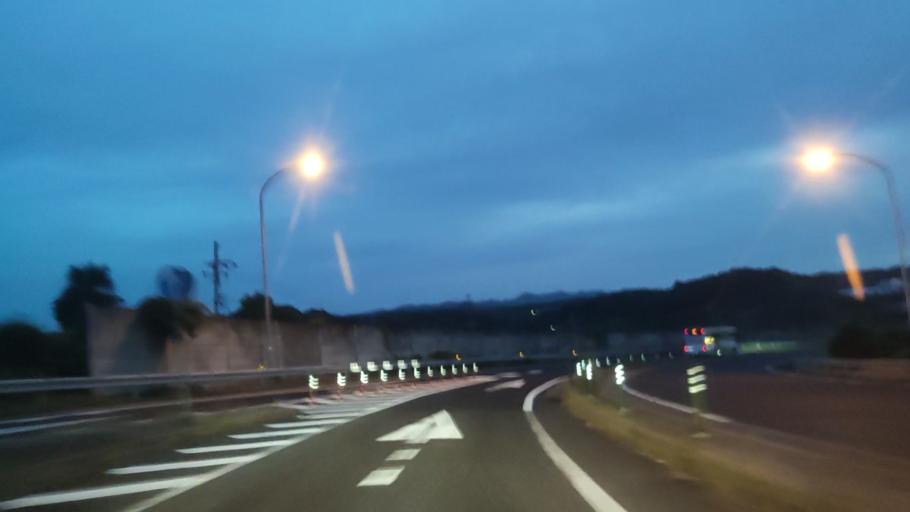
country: JP
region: Hyogo
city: Sandacho
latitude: 34.8884
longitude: 135.1179
